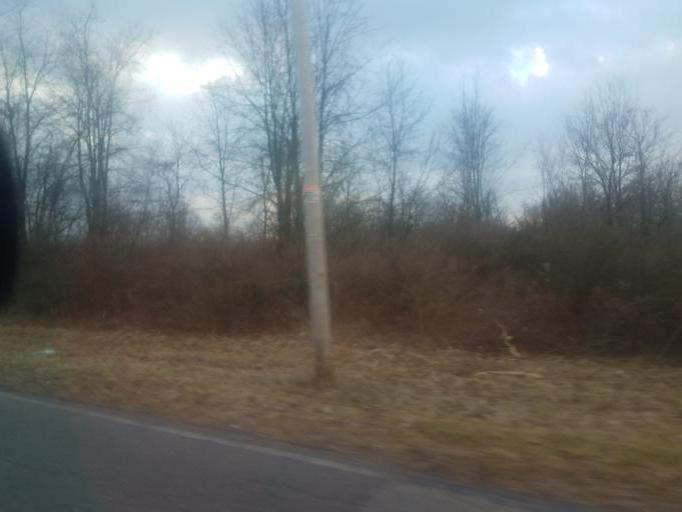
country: US
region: Ohio
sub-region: Marion County
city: Marion
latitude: 40.5930
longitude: -83.1629
